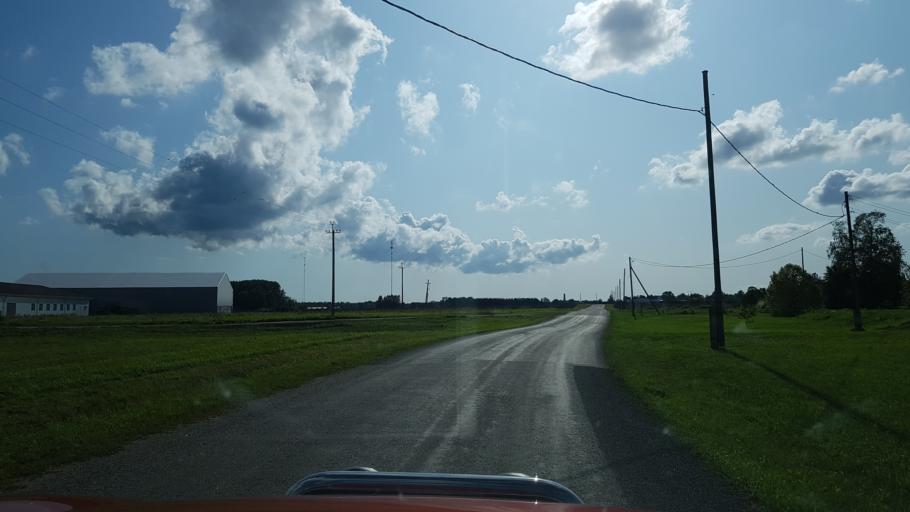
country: EE
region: Harju
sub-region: Paldiski linn
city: Paldiski
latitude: 59.2350
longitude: 24.0190
